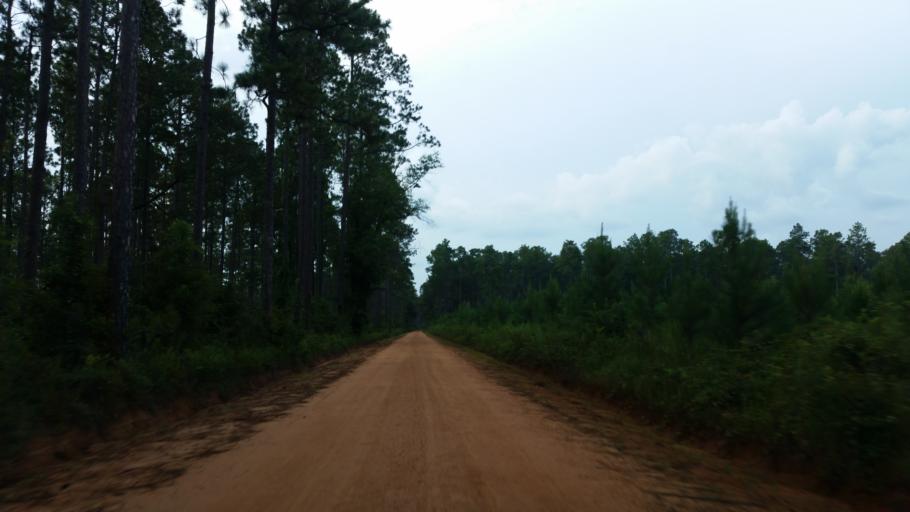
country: US
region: Alabama
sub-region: Baldwin County
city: Bay Minette
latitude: 30.8139
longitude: -87.5644
